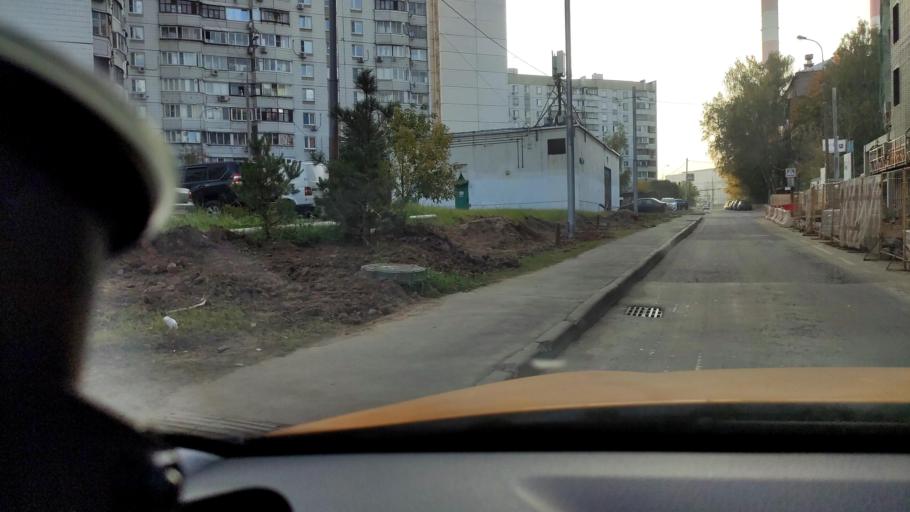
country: RU
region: Moscow
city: Metrogorodok
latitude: 55.8262
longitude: 37.7649
